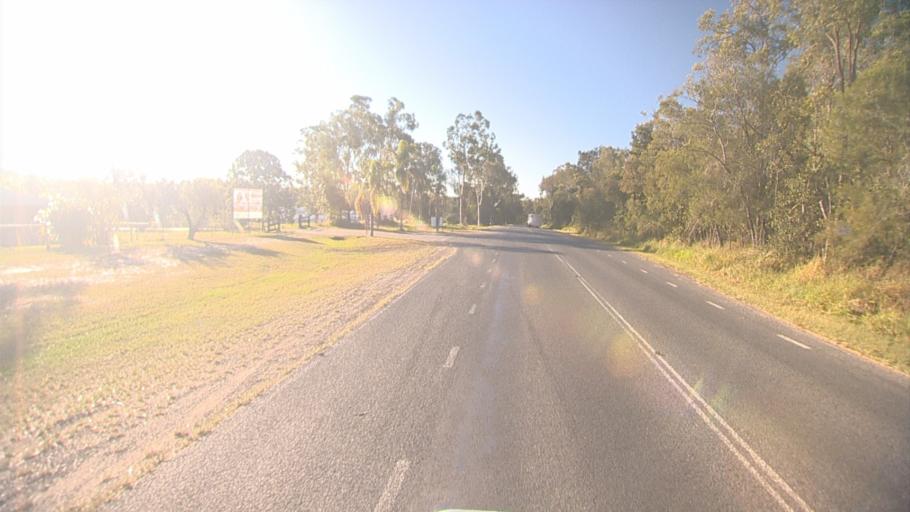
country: AU
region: Queensland
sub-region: Logan
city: Logan Reserve
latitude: -27.7258
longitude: 153.0900
